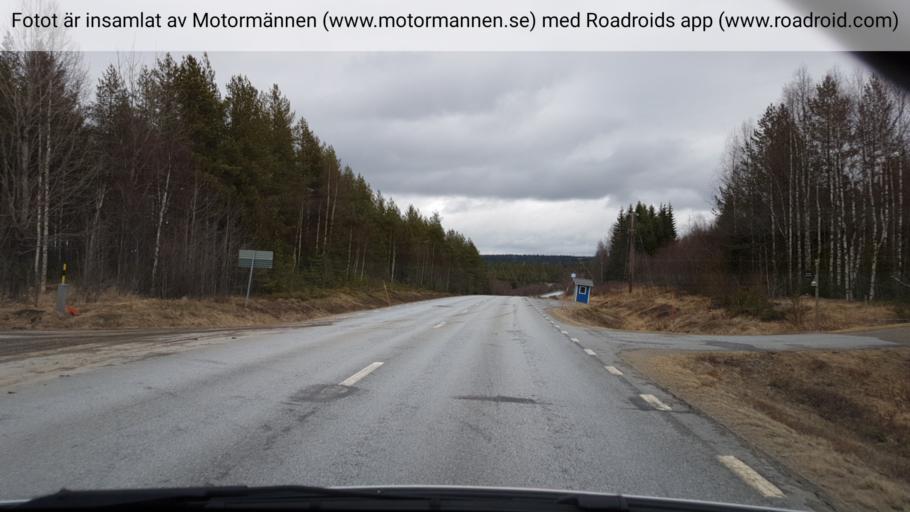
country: SE
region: Vaesterbotten
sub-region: Bjurholms Kommun
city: Bjurholm
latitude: 63.9370
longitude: 19.4141
